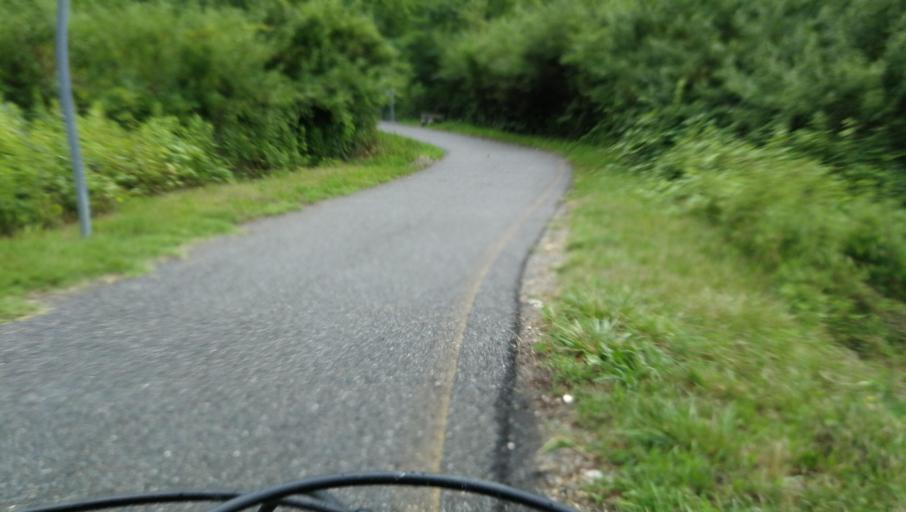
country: IT
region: Lombardy
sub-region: Provincia di Varese
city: Cittiglio
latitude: 45.8935
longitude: 8.6546
